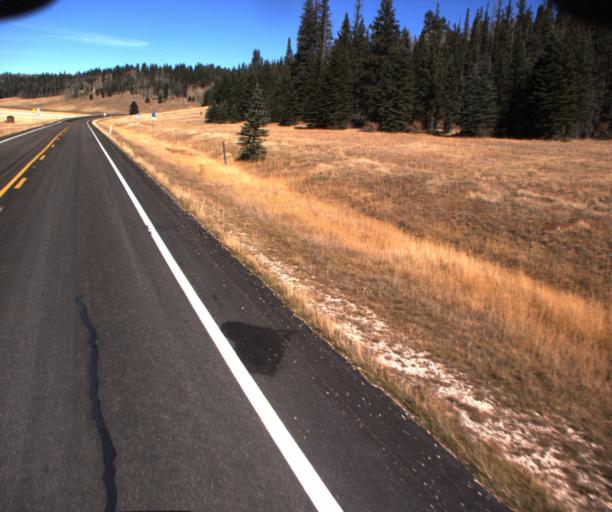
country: US
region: Arizona
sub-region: Coconino County
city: Grand Canyon
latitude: 36.4145
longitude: -112.1310
